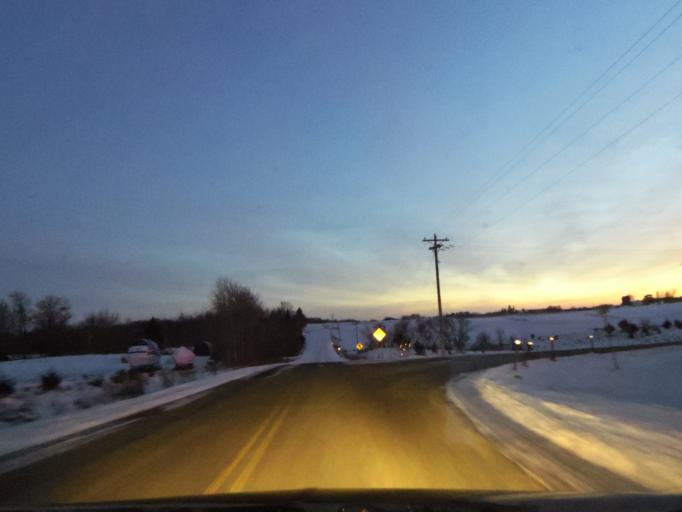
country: US
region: Minnesota
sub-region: Chisago County
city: Shafer
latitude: 45.3587
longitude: -92.7812
